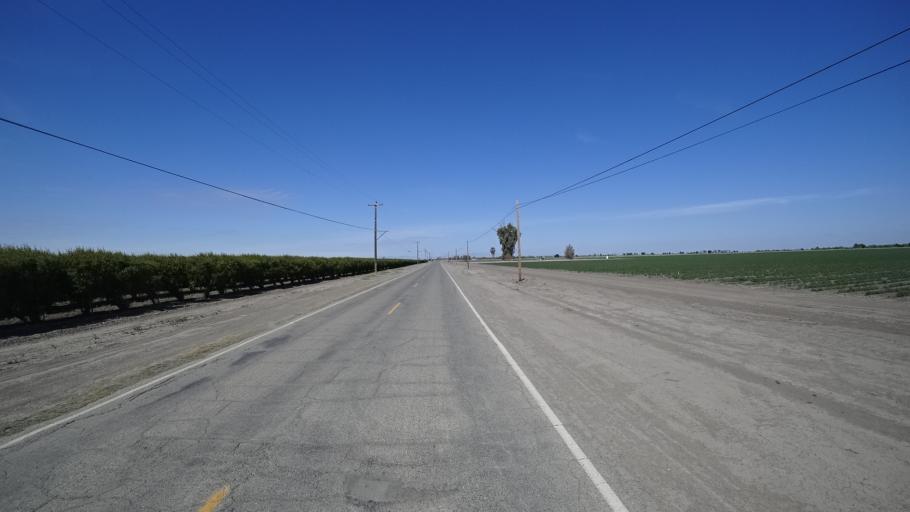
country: US
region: California
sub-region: Kings County
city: Lemoore Station
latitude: 36.2553
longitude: -119.8378
